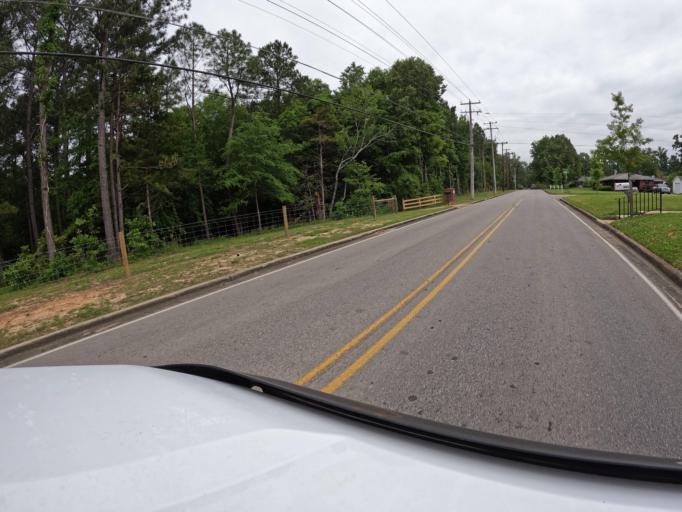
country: US
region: Mississippi
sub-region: Lee County
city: Tupelo
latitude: 34.2703
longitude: -88.7378
